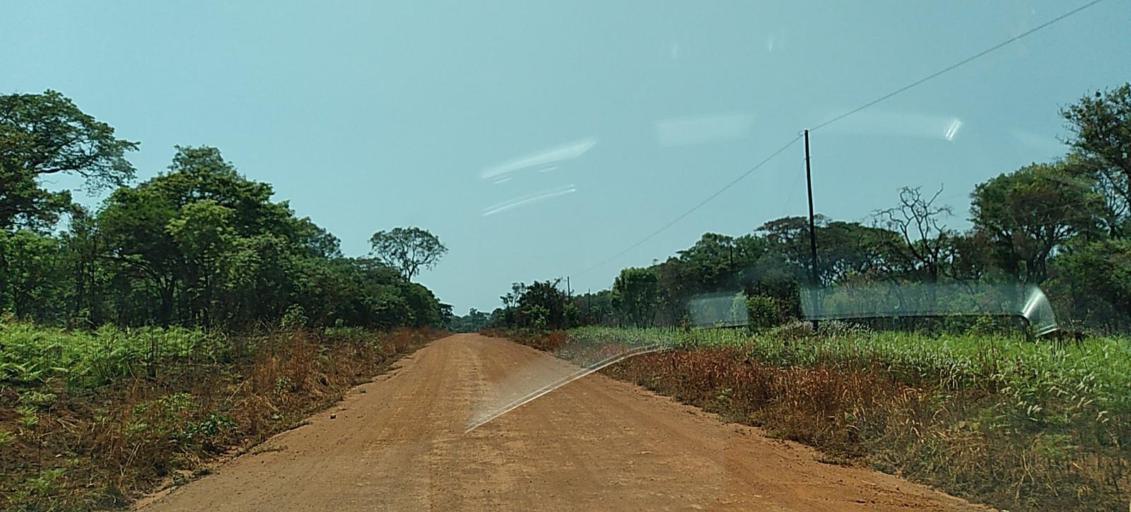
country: CD
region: Katanga
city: Kipushi
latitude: -11.9849
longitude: 26.8674
